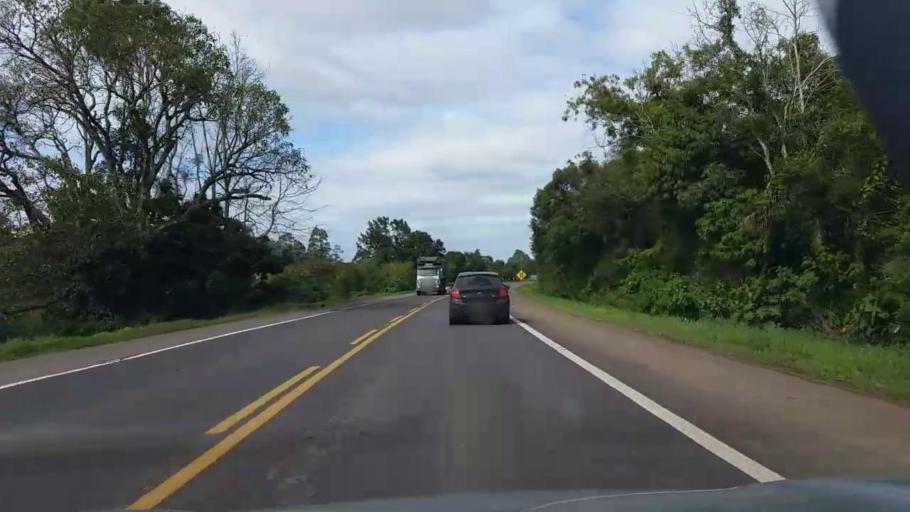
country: BR
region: Rio Grande do Sul
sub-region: Arroio Do Meio
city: Arroio do Meio
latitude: -29.3428
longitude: -52.0752
